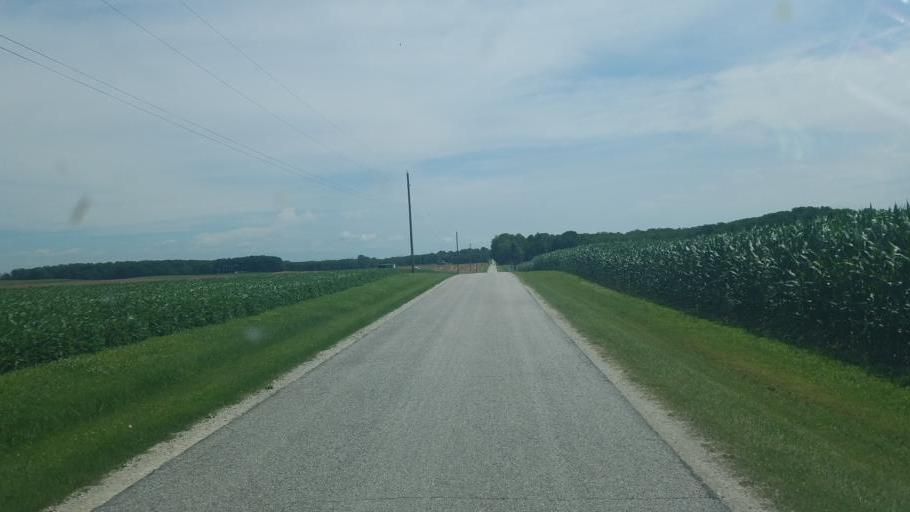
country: US
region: Ohio
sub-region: Crawford County
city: Bucyrus
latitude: 40.8709
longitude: -82.8966
